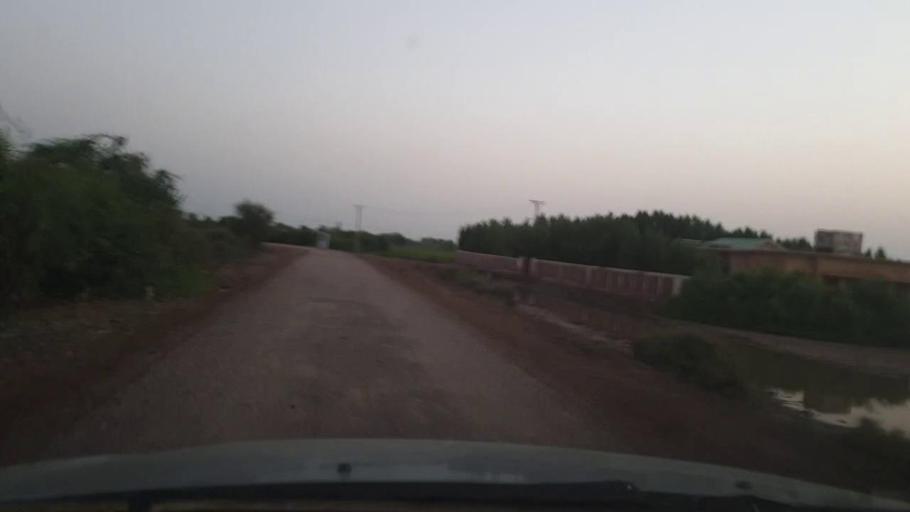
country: PK
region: Sindh
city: Digri
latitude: 25.1215
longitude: 69.0055
